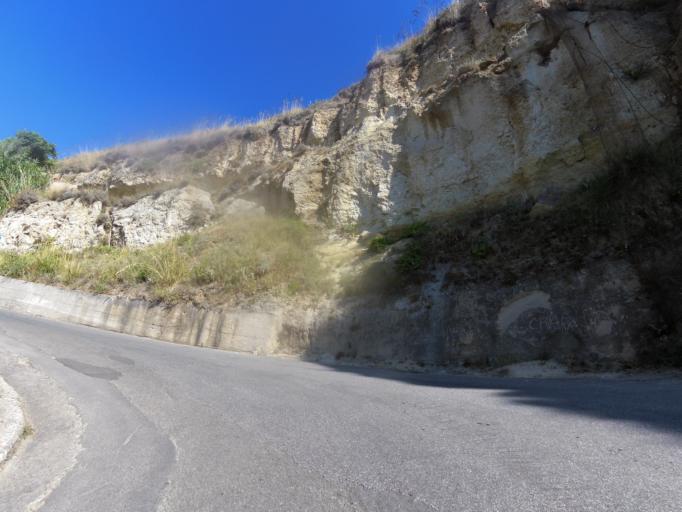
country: IT
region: Calabria
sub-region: Provincia di Vibo-Valentia
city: Santa Domenica
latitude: 38.6697
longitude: 15.8691
